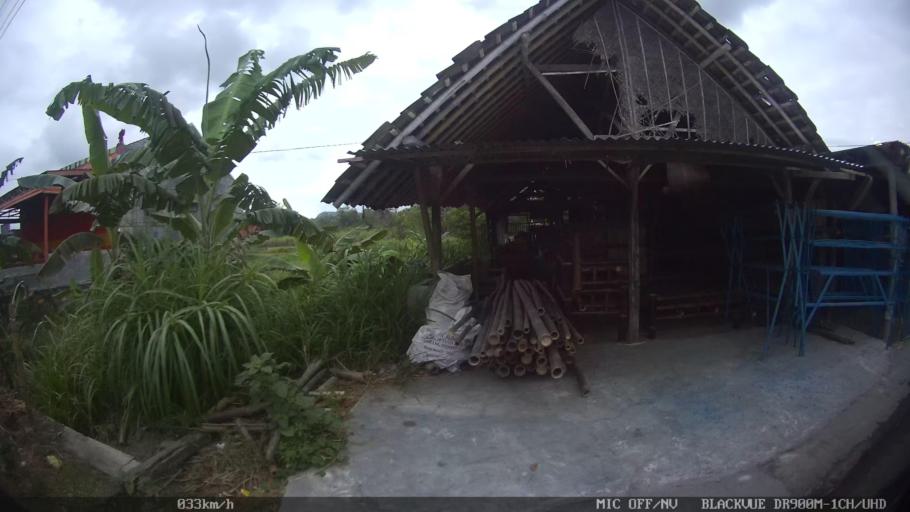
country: ID
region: Daerah Istimewa Yogyakarta
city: Sewon
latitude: -7.8728
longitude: 110.4073
